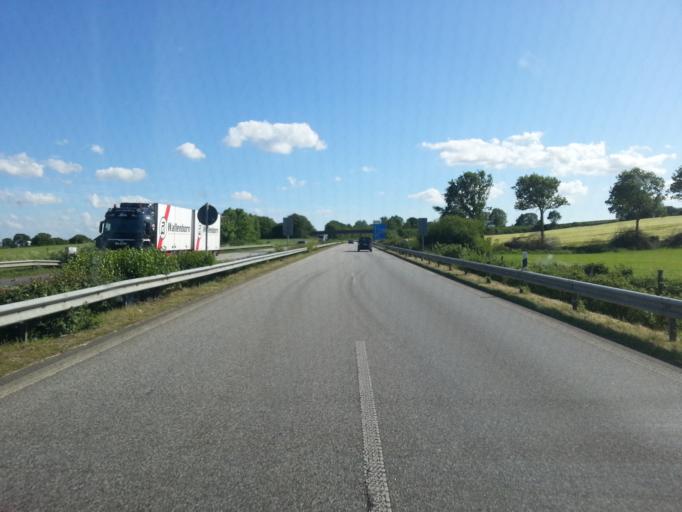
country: DE
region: Schleswig-Holstein
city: Neustadt in Holstein
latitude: 54.1042
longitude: 10.7811
